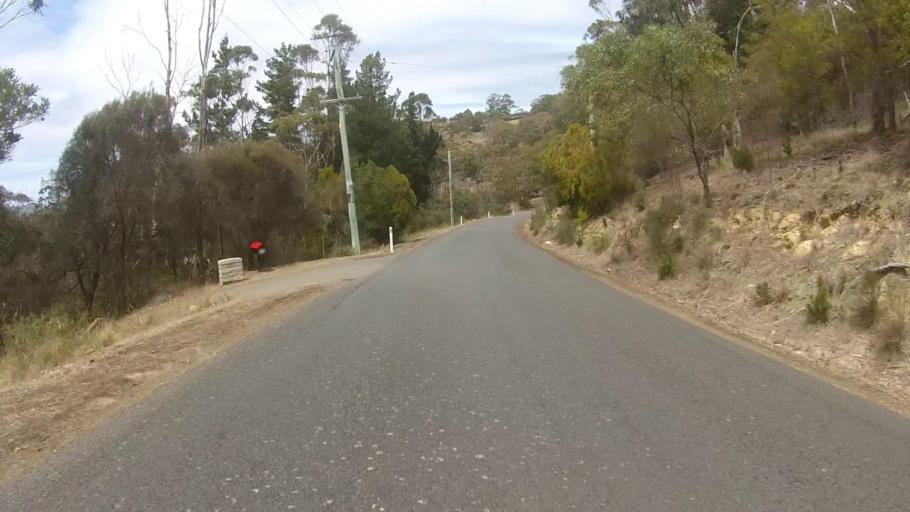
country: AU
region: Tasmania
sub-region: Kingborough
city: Blackmans Bay
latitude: -43.0343
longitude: 147.3323
